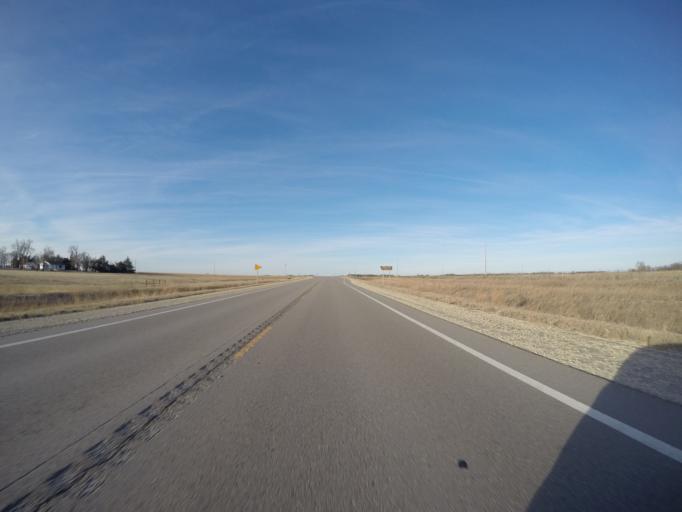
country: US
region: Kansas
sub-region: Marion County
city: Marion
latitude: 38.3175
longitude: -96.9666
